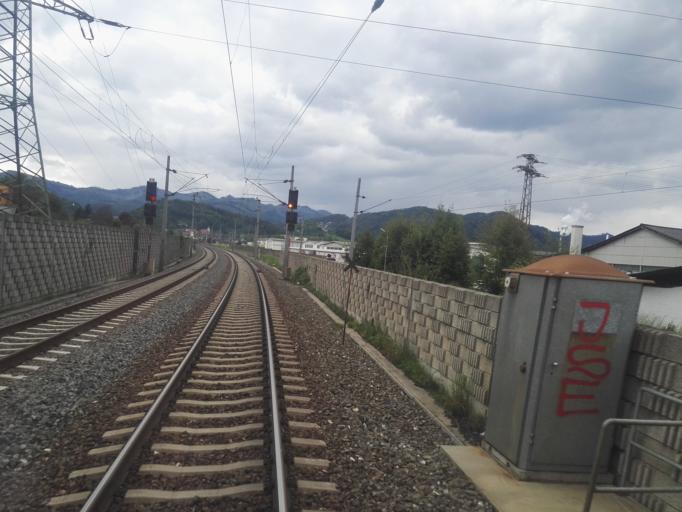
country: AT
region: Styria
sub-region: Politischer Bezirk Graz-Umgebung
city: Gratkorn
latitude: 47.1233
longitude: 15.3352
